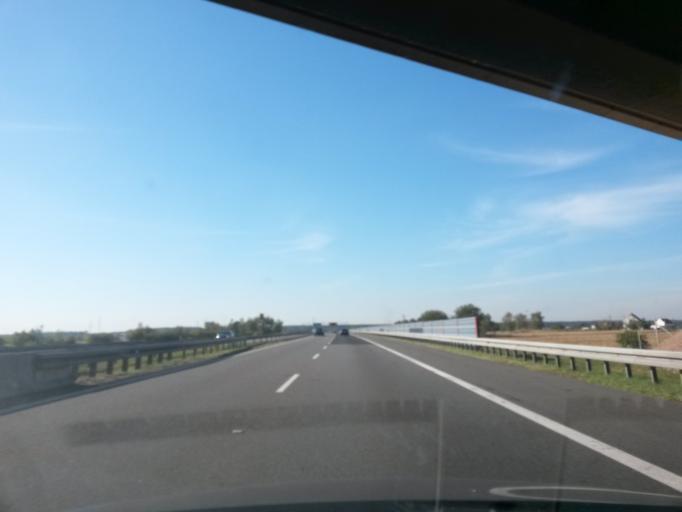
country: PL
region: Opole Voivodeship
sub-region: Powiat krapkowicki
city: Krapkowice
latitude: 50.5240
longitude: 17.9351
